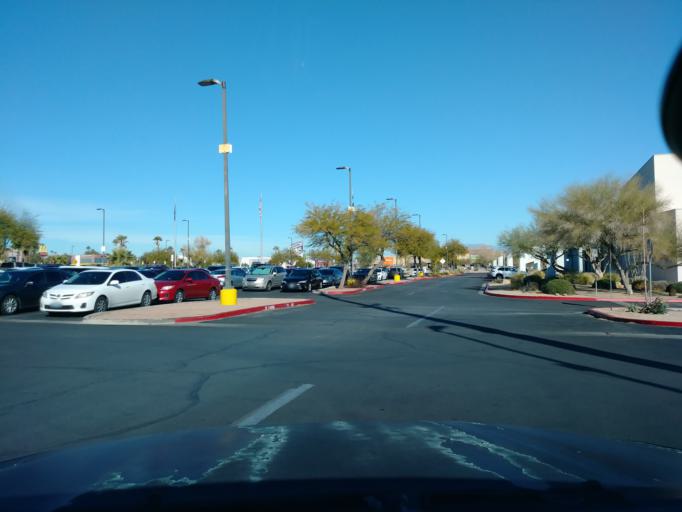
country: US
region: Nevada
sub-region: Clark County
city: Spring Valley
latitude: 36.1574
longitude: -115.2316
